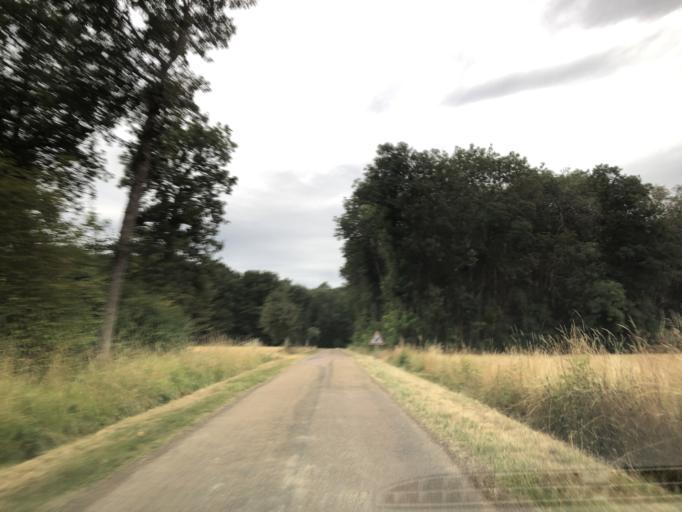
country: FR
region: Bourgogne
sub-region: Departement de l'Yonne
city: Aillant-sur-Tholon
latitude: 47.9001
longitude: 3.3028
